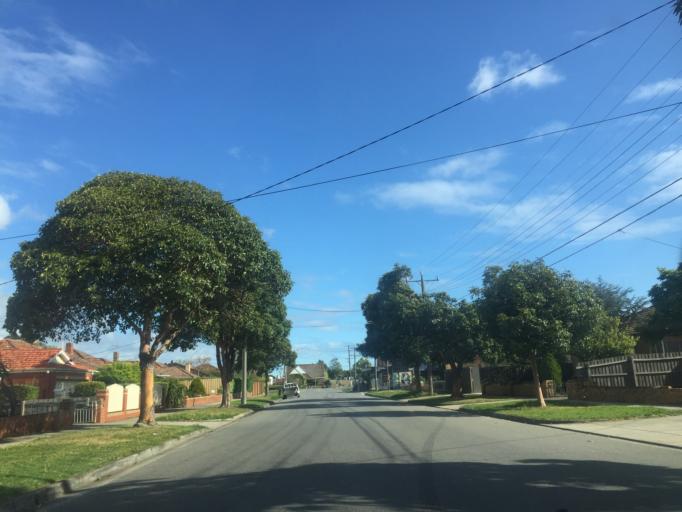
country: AU
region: Victoria
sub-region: Darebin
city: Reservoir
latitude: -37.7232
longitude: 145.0158
